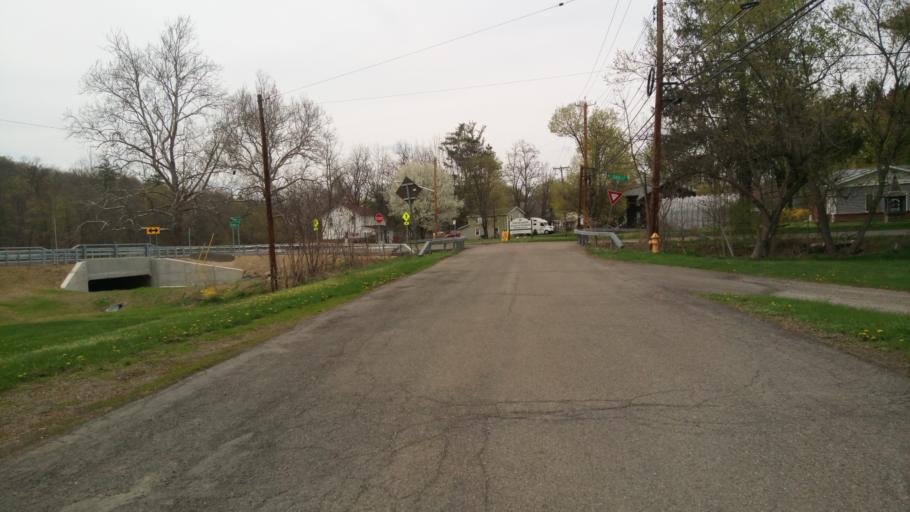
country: US
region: New York
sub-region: Chemung County
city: Southport
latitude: 42.0099
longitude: -76.7286
